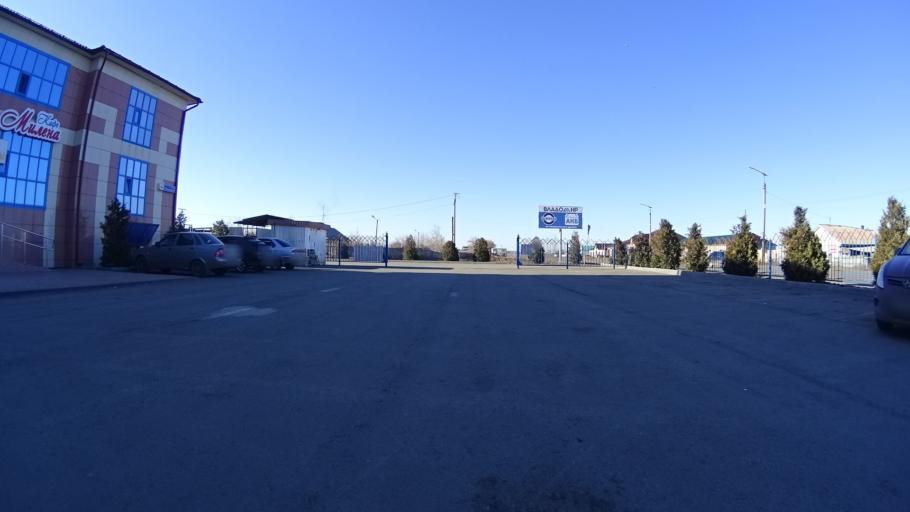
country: RU
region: Chelyabinsk
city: Troitsk
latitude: 54.0832
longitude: 61.5112
